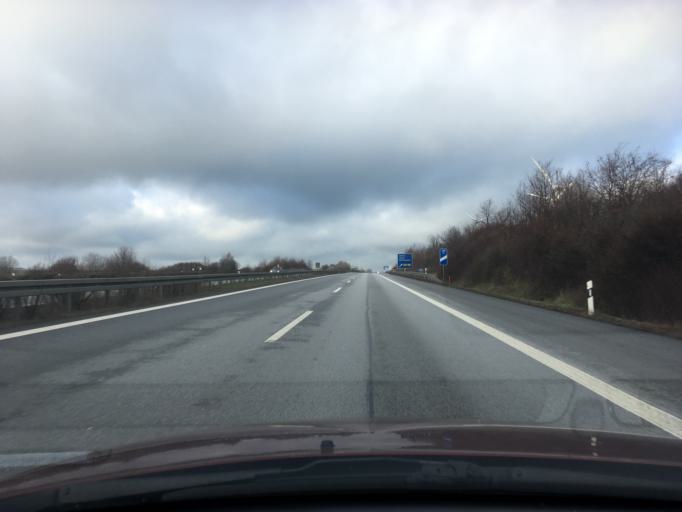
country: DE
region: Saxony
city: Goerlitz
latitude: 51.1965
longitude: 14.9664
